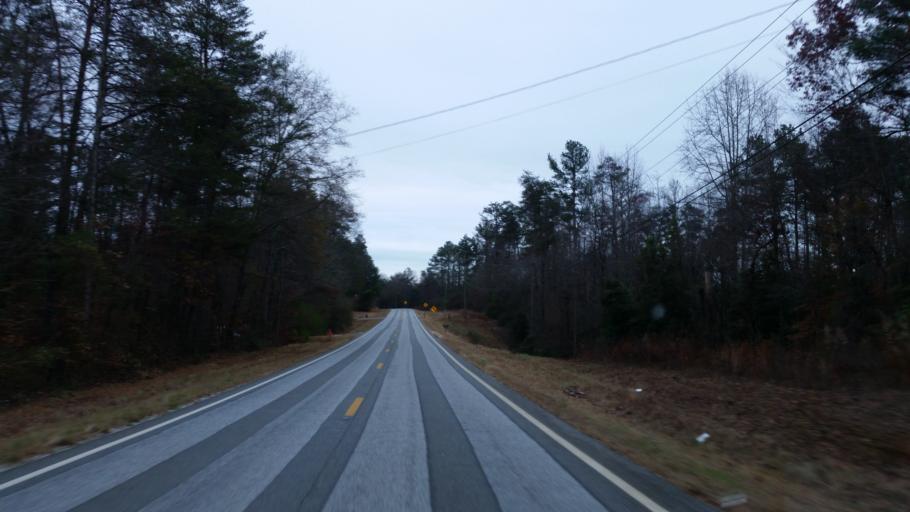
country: US
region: Georgia
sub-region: Dawson County
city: Dawsonville
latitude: 34.4992
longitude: -84.2024
